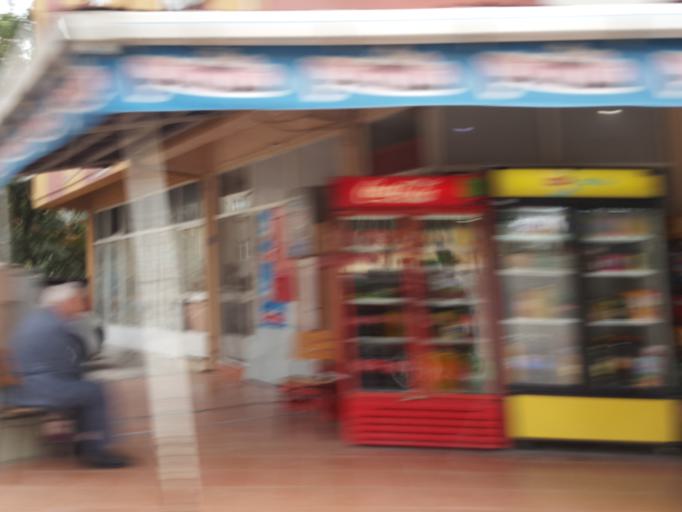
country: TR
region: Sinop
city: Duragan
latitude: 41.4195
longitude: 35.0535
